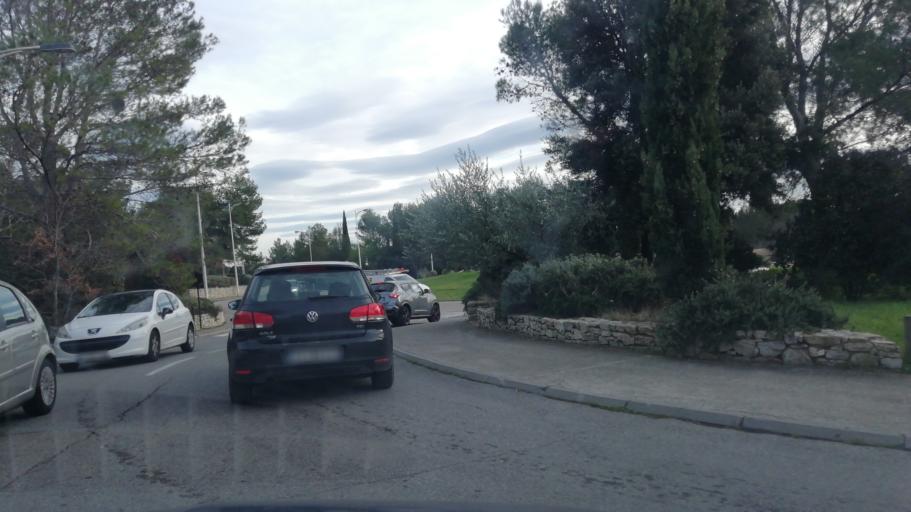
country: FR
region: Languedoc-Roussillon
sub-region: Departement du Gard
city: Nimes
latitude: 43.8442
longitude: 4.3082
